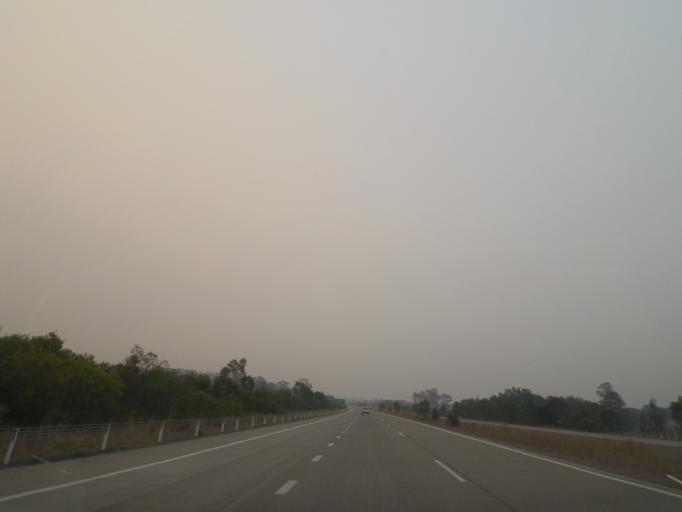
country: AU
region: New South Wales
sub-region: Kempsey
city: Frederickton
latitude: -31.0239
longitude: 152.8795
